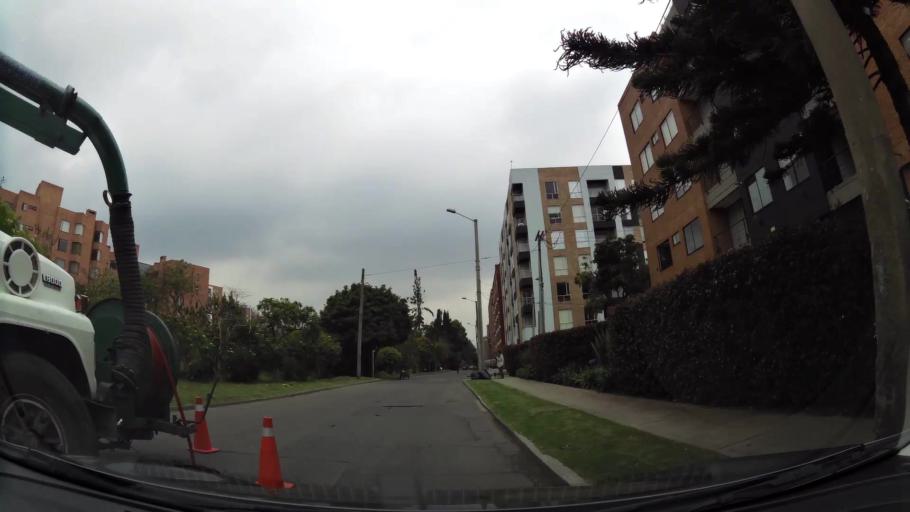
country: CO
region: Bogota D.C.
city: Barrio San Luis
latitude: 4.7261
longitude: -74.0414
